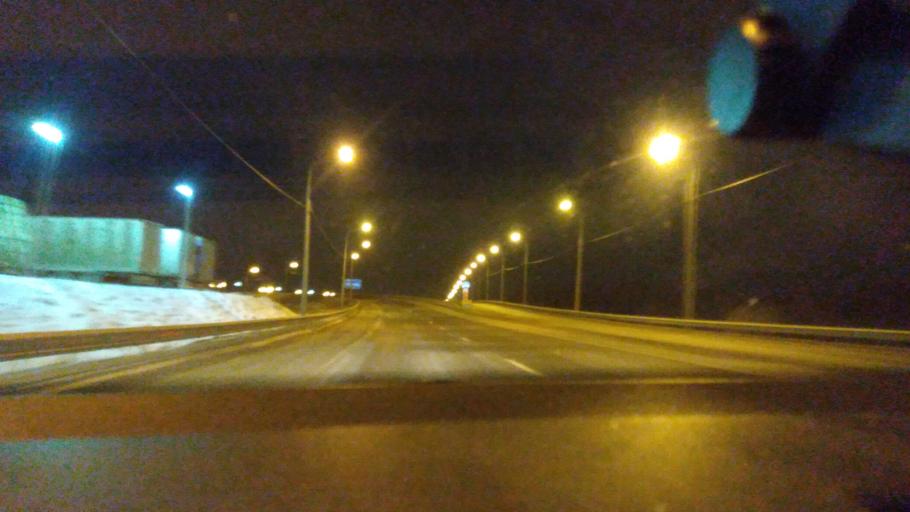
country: RU
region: Moskovskaya
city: Raduzhnyy
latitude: 55.1640
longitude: 38.6797
